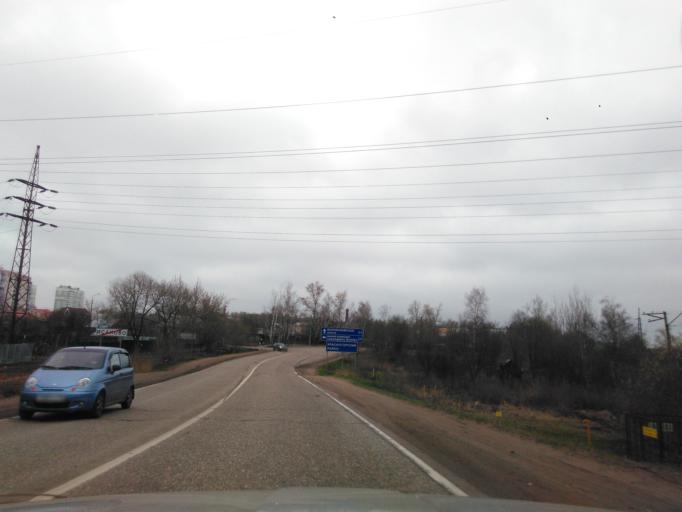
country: RU
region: Moskovskaya
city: Nakhabino
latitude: 55.8334
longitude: 37.1545
